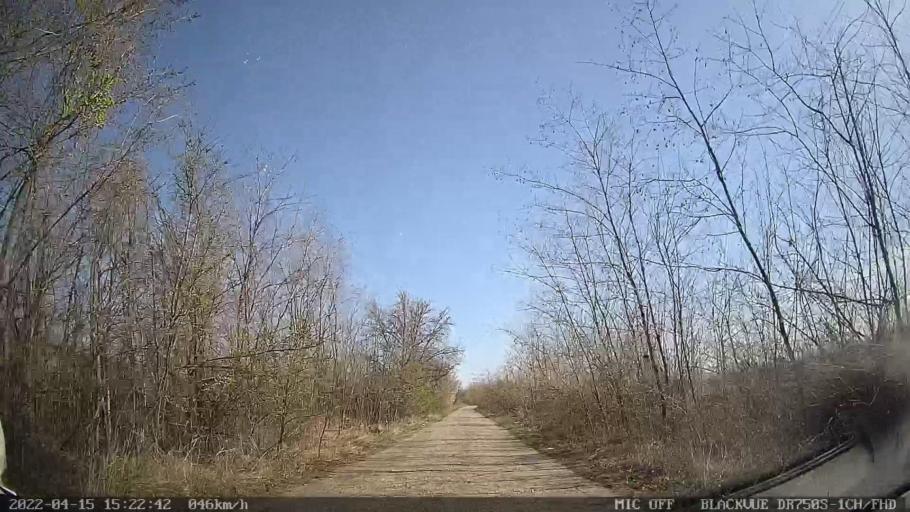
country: MD
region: Raionul Ocnita
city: Otaci
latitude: 48.3795
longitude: 27.9154
